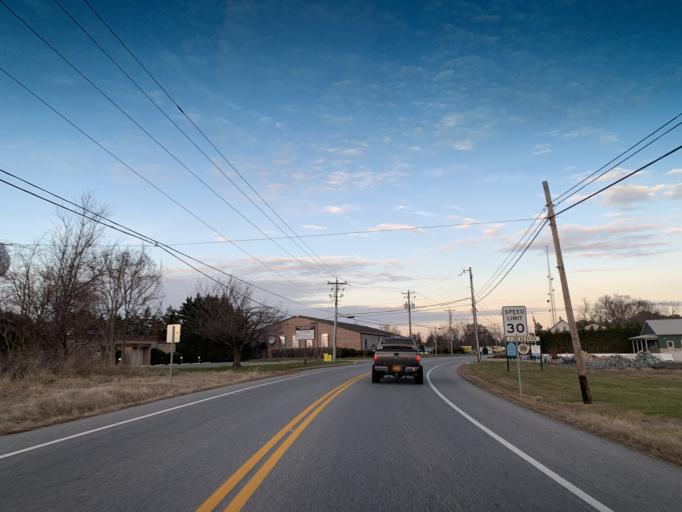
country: US
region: Delaware
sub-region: New Castle County
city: Middletown
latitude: 39.3993
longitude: -75.8712
